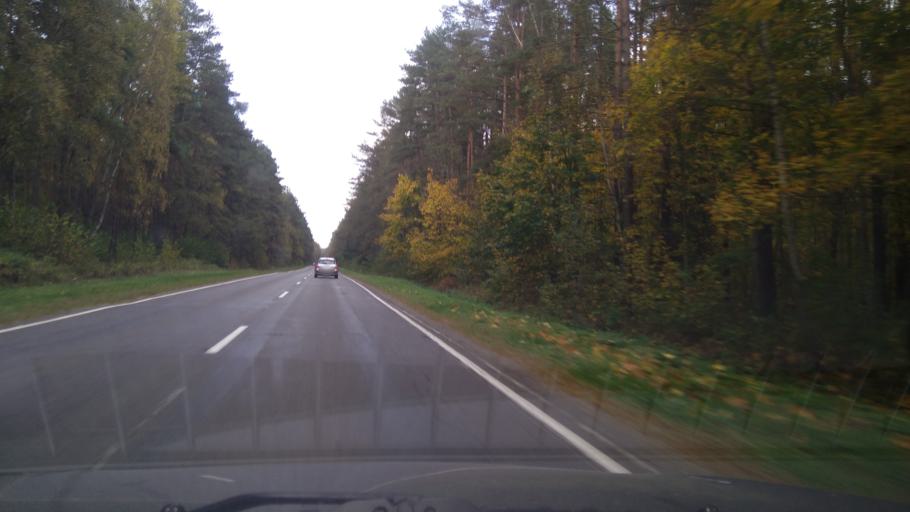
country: BY
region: Minsk
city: Druzhny
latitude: 53.6276
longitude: 27.8760
